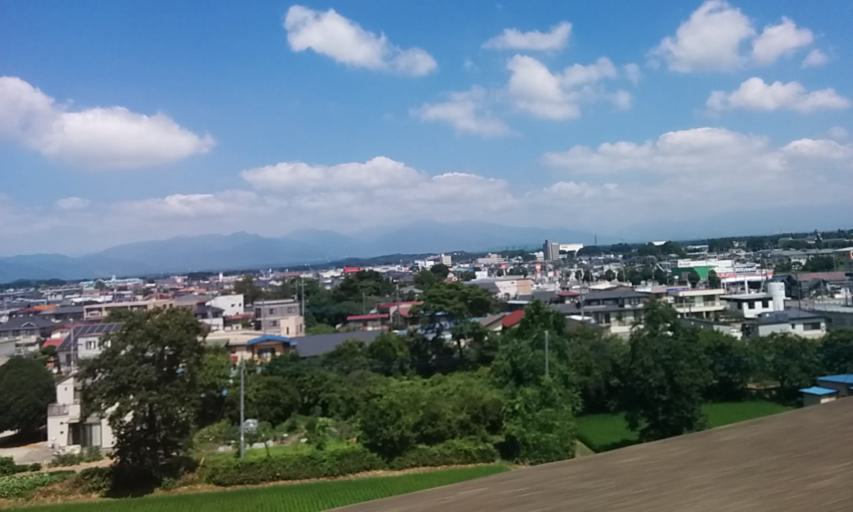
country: JP
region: Tochigi
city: Otawara
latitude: 36.8879
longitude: 139.9891
